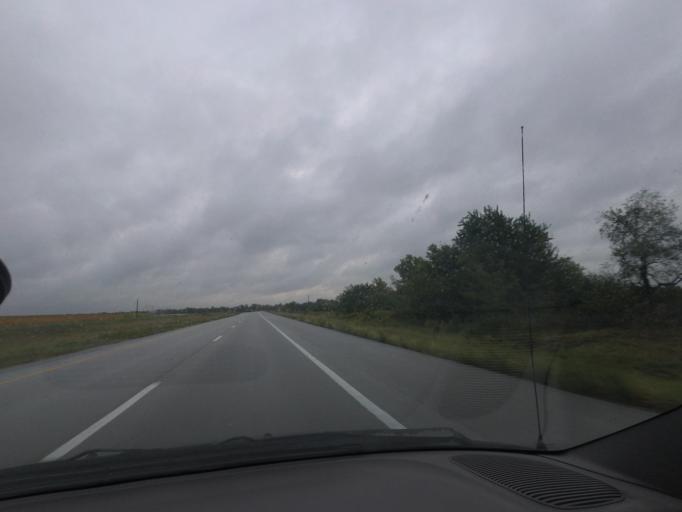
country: US
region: Missouri
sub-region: Marion County
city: Monroe City
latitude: 39.6646
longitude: -91.6810
